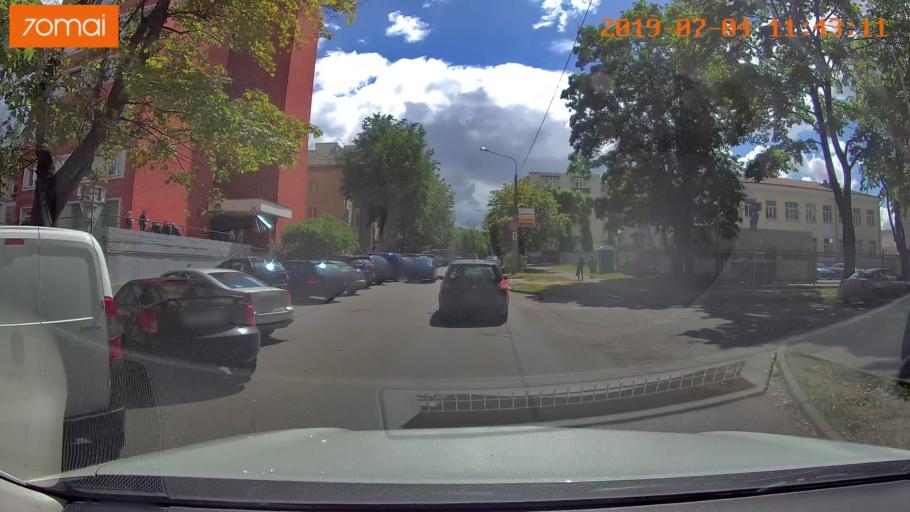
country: BY
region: Minsk
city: Minsk
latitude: 53.9276
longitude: 27.5991
